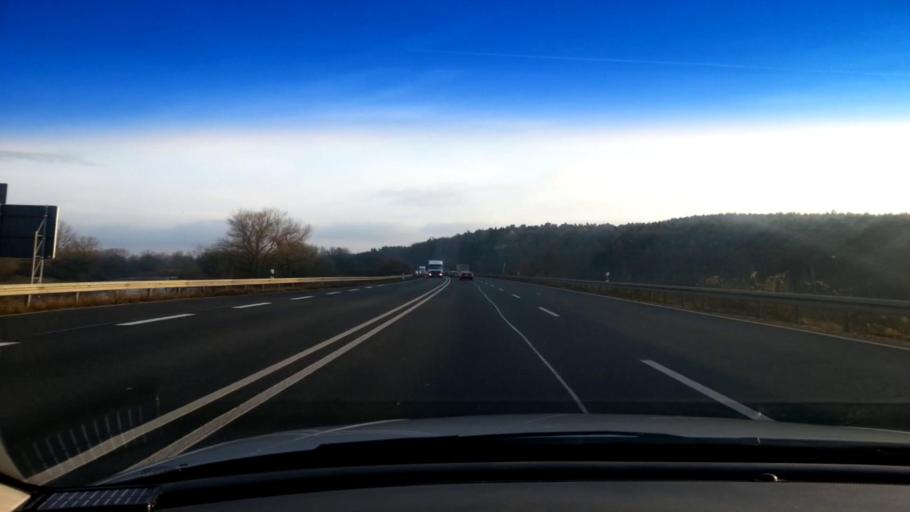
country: DE
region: Bavaria
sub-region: Upper Franconia
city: Pettstadt
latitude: 49.8274
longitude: 10.9519
